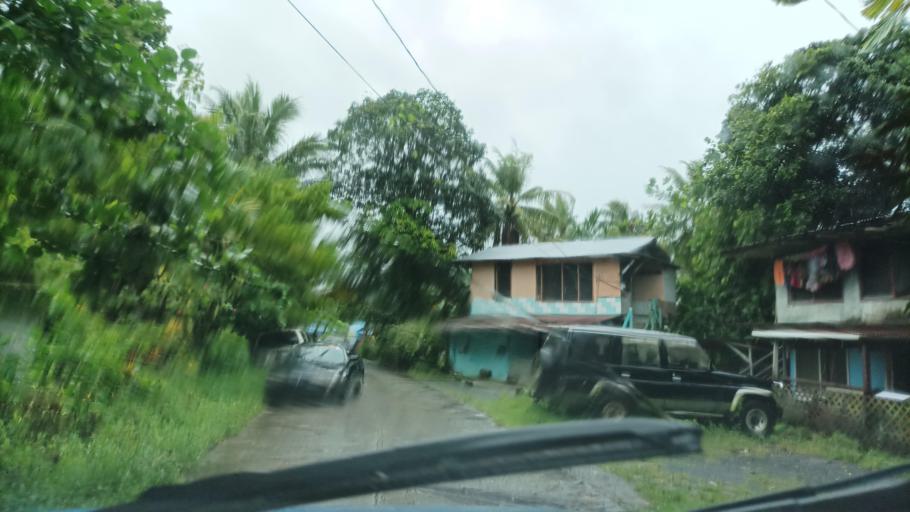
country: FM
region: Pohnpei
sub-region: Kolonia Municipality
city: Kolonia
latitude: 6.9691
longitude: 158.2070
